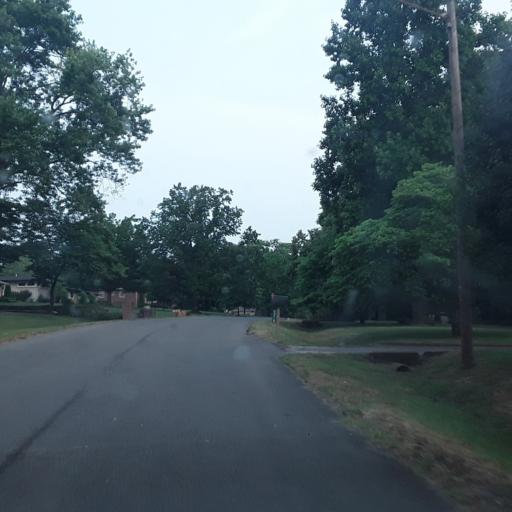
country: US
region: Tennessee
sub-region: Williamson County
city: Brentwood
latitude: 36.0578
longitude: -86.7646
